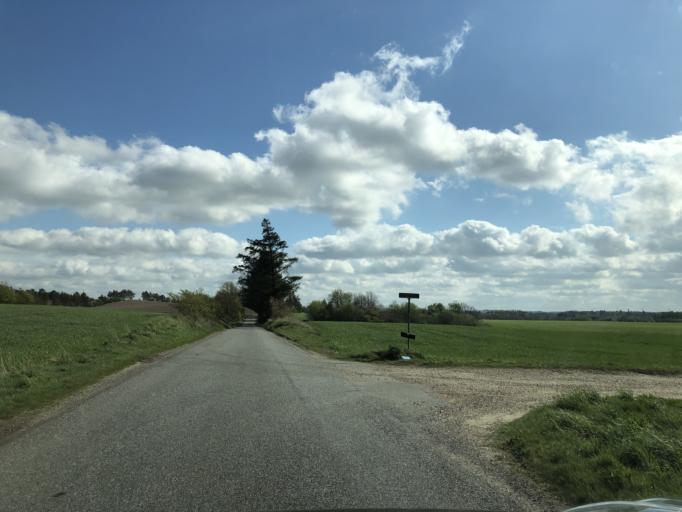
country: DK
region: Central Jutland
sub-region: Herning Kommune
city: Avlum
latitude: 56.2839
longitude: 8.6979
